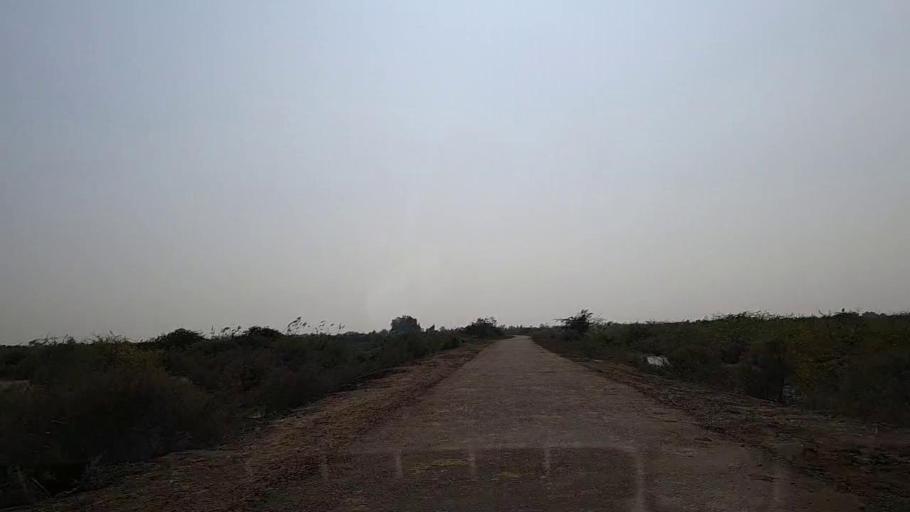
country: PK
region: Sindh
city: Mirpur Sakro
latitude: 24.6538
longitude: 67.6909
